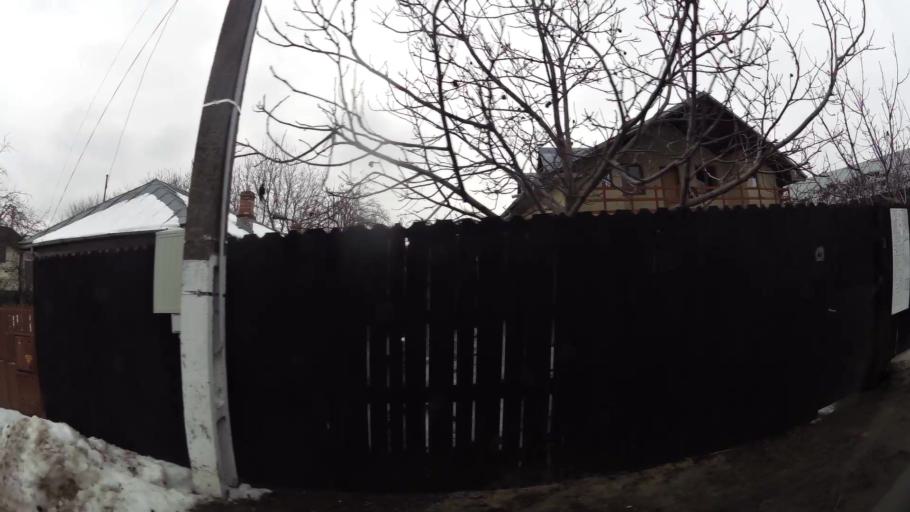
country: RO
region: Ilfov
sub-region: Comuna Tunari
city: Tunari
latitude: 44.5473
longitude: 26.1290
